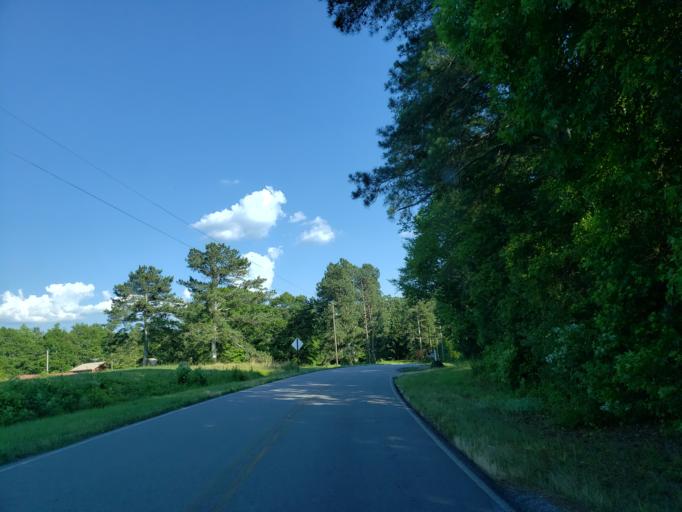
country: US
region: Georgia
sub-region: Haralson County
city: Bremen
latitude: 33.6834
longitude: -85.0883
